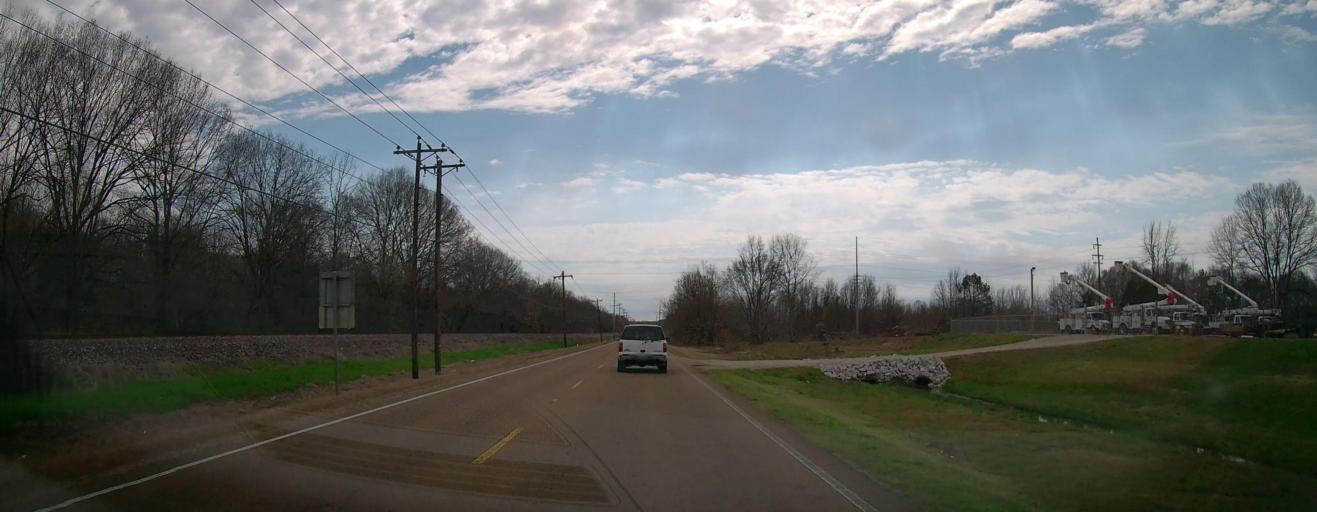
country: US
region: Mississippi
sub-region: Marshall County
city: Byhalia
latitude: 34.9128
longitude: -89.7615
